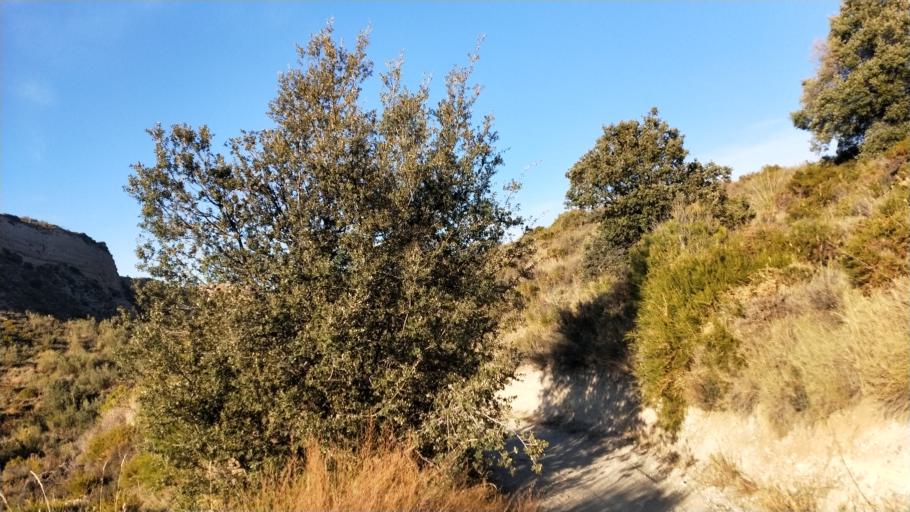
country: ES
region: Andalusia
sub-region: Provincia de Granada
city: Dudar
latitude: 37.1953
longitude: -3.5011
